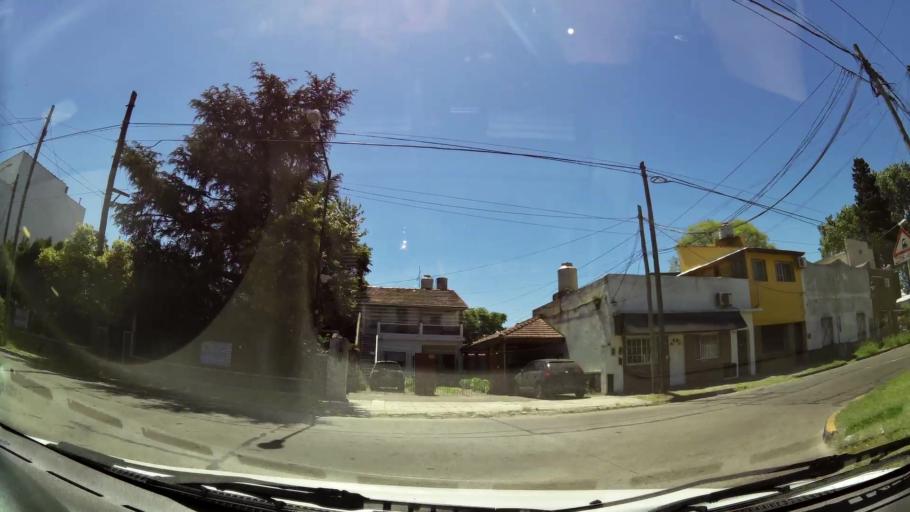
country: AR
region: Buenos Aires
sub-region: Partido de General San Martin
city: General San Martin
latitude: -34.5217
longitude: -58.5499
